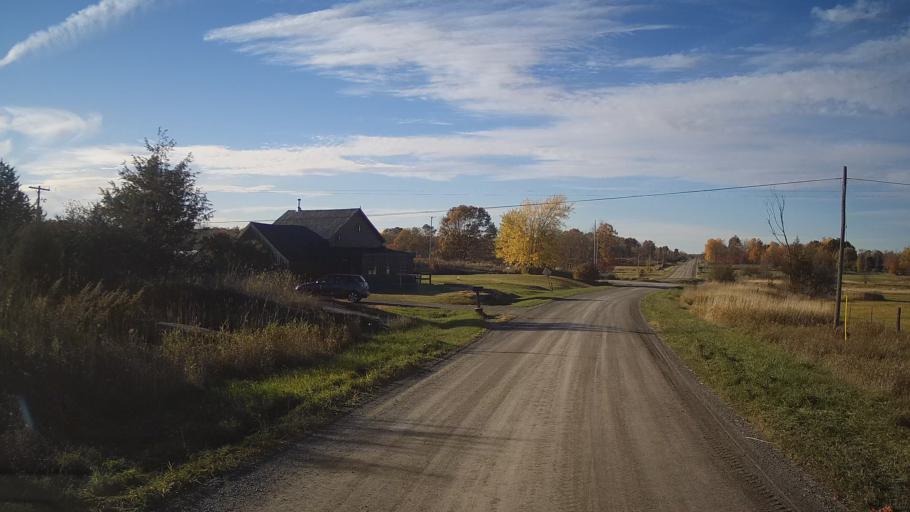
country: CA
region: Ontario
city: Perth
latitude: 44.7060
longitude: -76.4293
